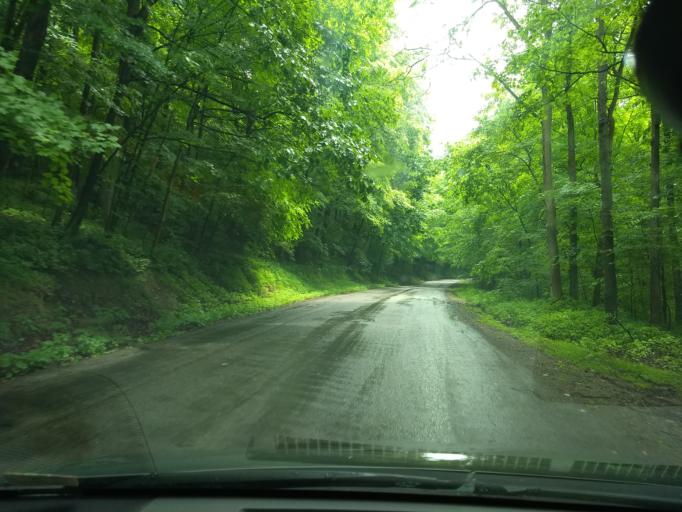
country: US
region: Pennsylvania
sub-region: Armstrong County
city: Orchard Hills
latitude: 40.5678
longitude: -79.5149
